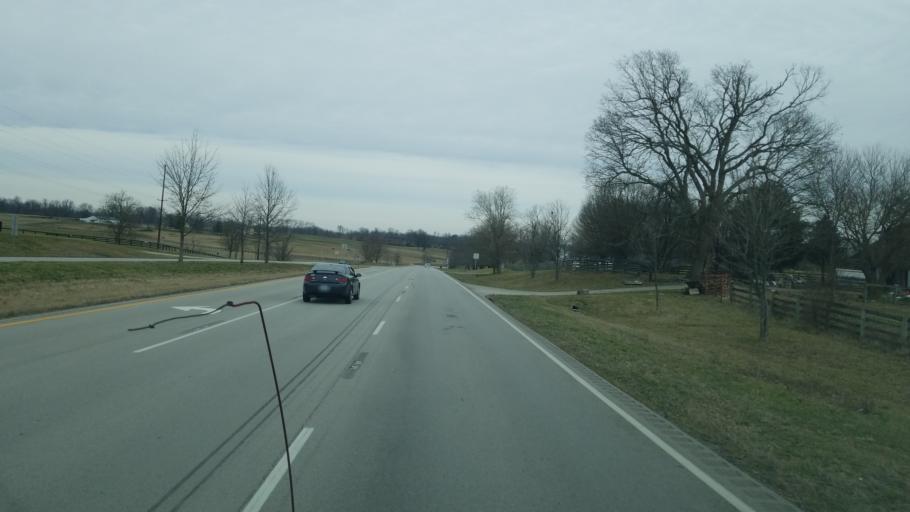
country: US
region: Kentucky
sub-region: Bourbon County
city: Paris
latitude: 38.1527
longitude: -84.3387
